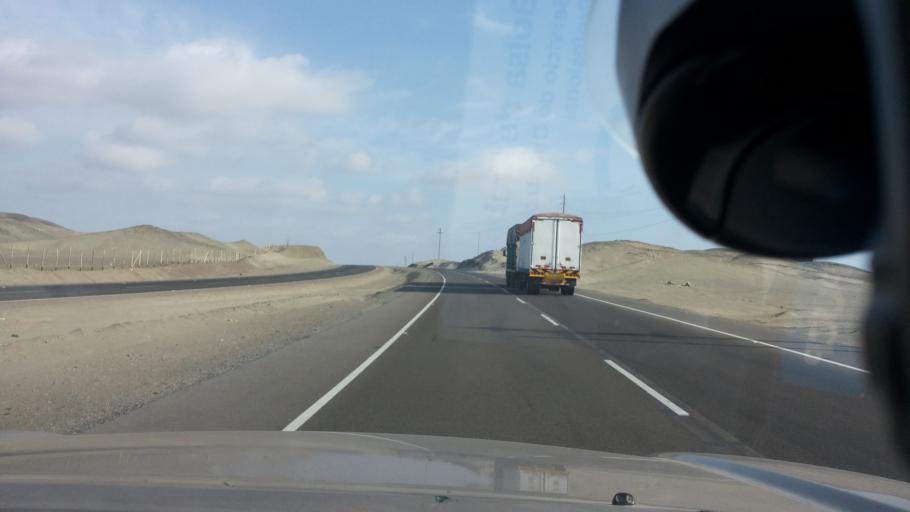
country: PE
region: Ancash
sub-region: Provincia de Huarmey
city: La Caleta Culebras
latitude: -10.0044
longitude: -78.1822
